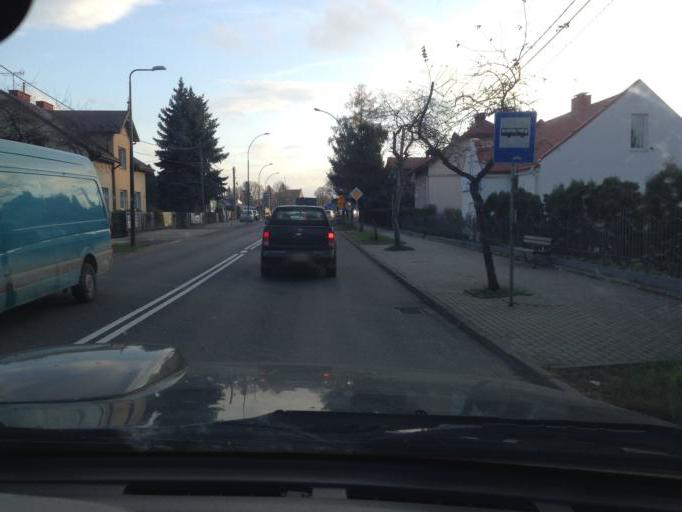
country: PL
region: Subcarpathian Voivodeship
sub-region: Powiat jasielski
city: Jaslo
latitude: 49.7537
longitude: 21.4736
